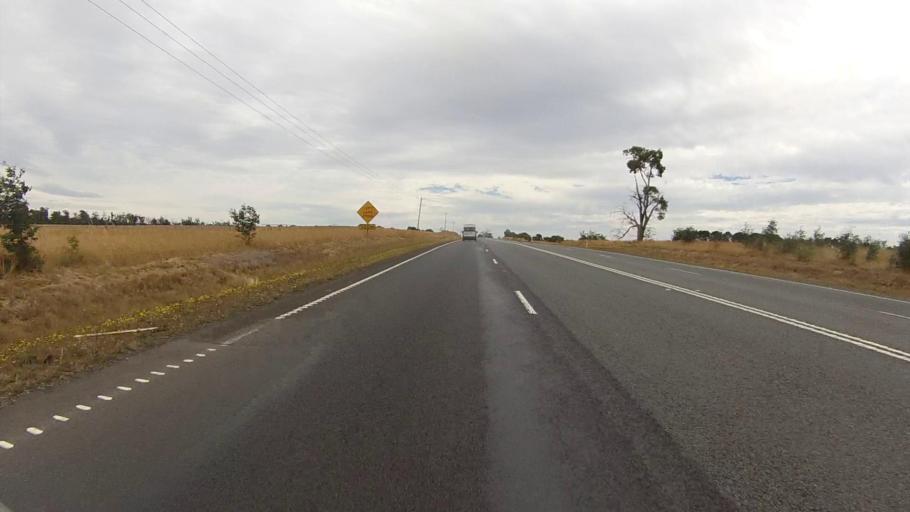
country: AU
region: Tasmania
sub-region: Northern Midlands
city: Evandale
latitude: -41.7134
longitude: 147.3044
